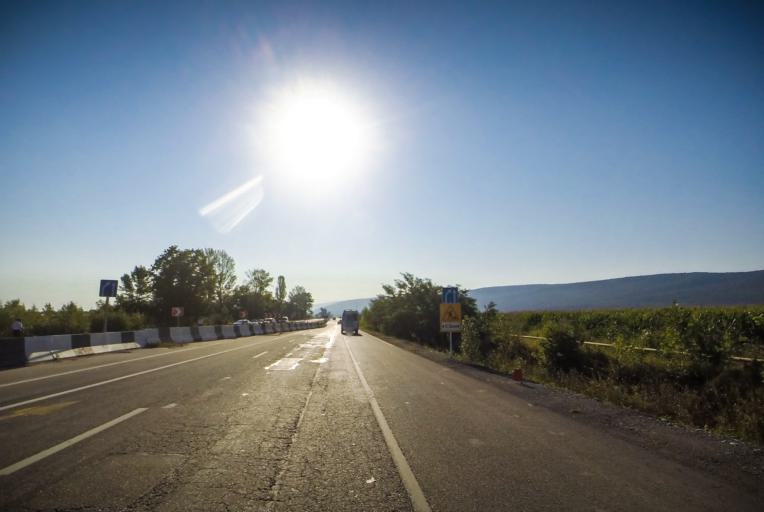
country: RU
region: North Ossetia
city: Zmeyskaya
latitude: 43.3230
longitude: 44.1272
